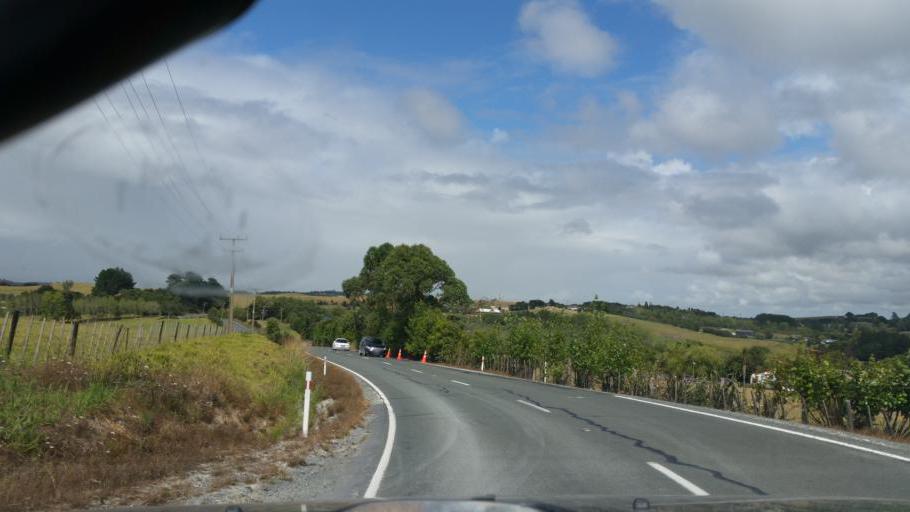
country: NZ
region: Auckland
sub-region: Auckland
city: Wellsford
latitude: -36.1047
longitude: 174.5541
